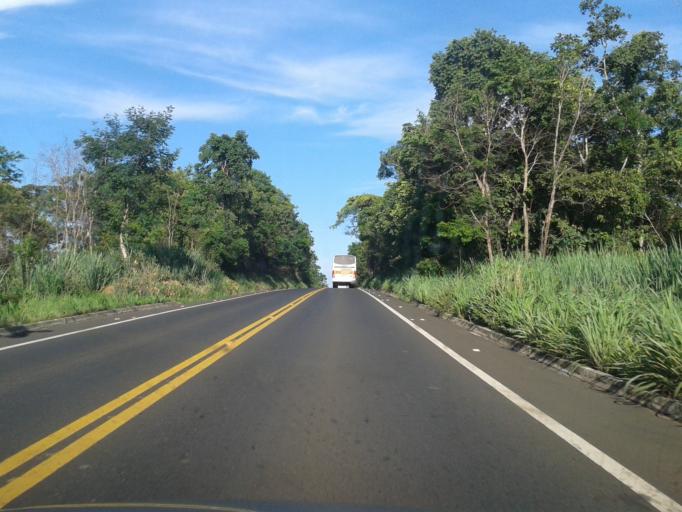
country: BR
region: Goias
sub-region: Caldas Novas
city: Caldas Novas
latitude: -18.1175
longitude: -48.5988
